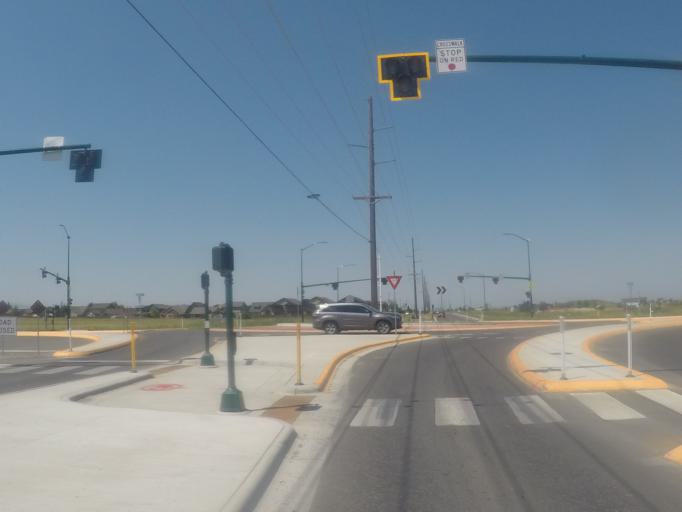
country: US
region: Montana
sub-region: Gallatin County
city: Bozeman
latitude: 45.6930
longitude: -111.0824
